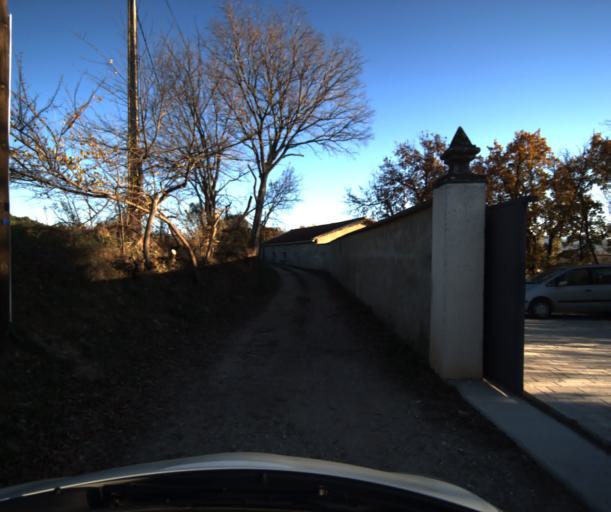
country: FR
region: Provence-Alpes-Cote d'Azur
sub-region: Departement du Vaucluse
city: Pertuis
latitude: 43.6856
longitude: 5.5100
